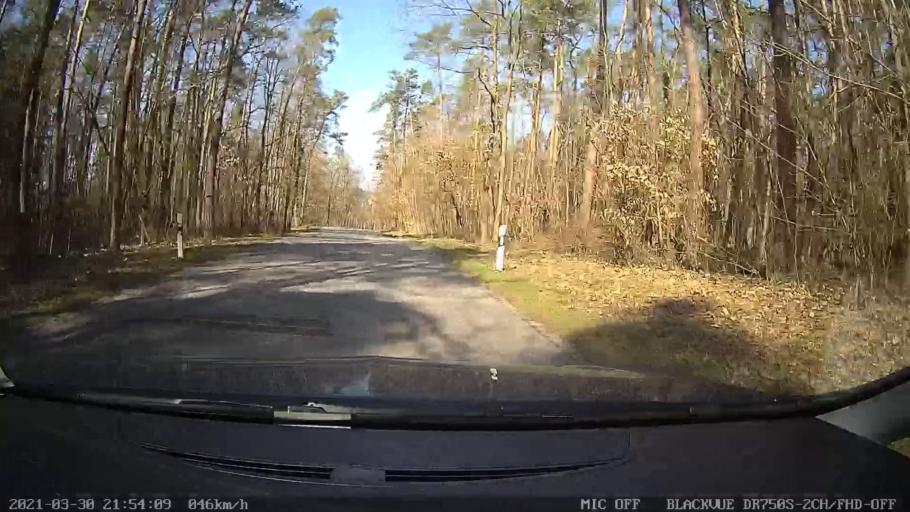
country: DE
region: Bavaria
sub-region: Upper Palatinate
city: Zeitlarn
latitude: 49.0945
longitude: 12.1166
